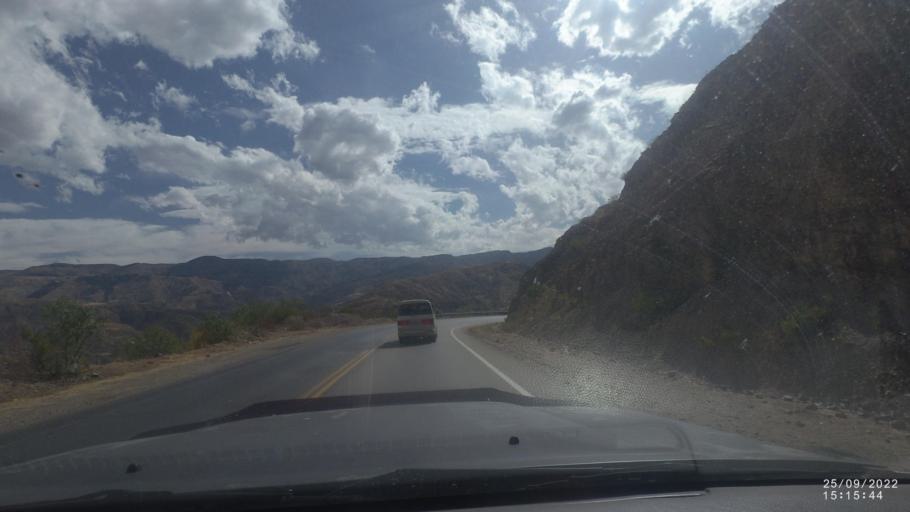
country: BO
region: Cochabamba
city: Irpa Irpa
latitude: -17.6319
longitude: -66.3916
